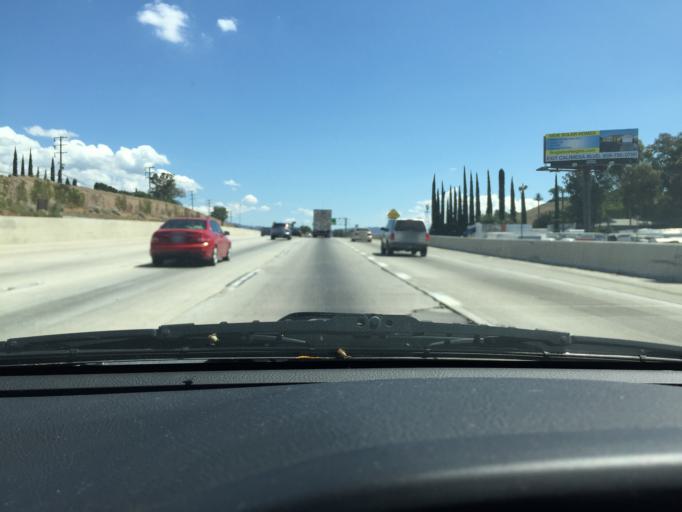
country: US
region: California
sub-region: San Bernardino County
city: Mentone
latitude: 34.0279
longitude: -117.1261
